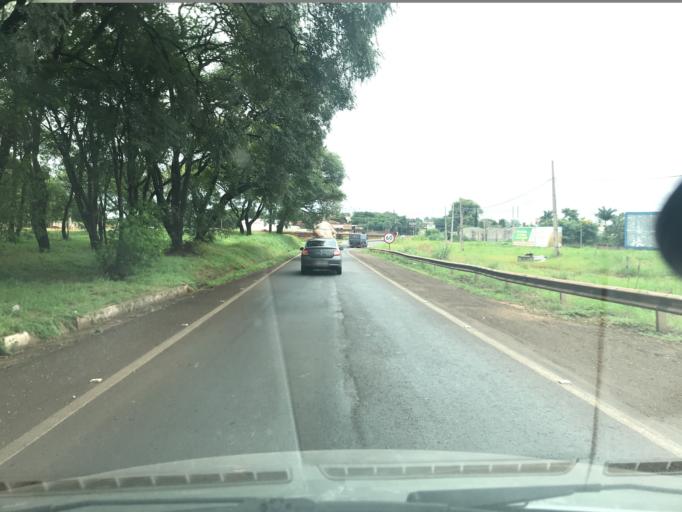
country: BR
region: Parana
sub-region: Maringa
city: Maringa
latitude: -23.4459
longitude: -51.9828
